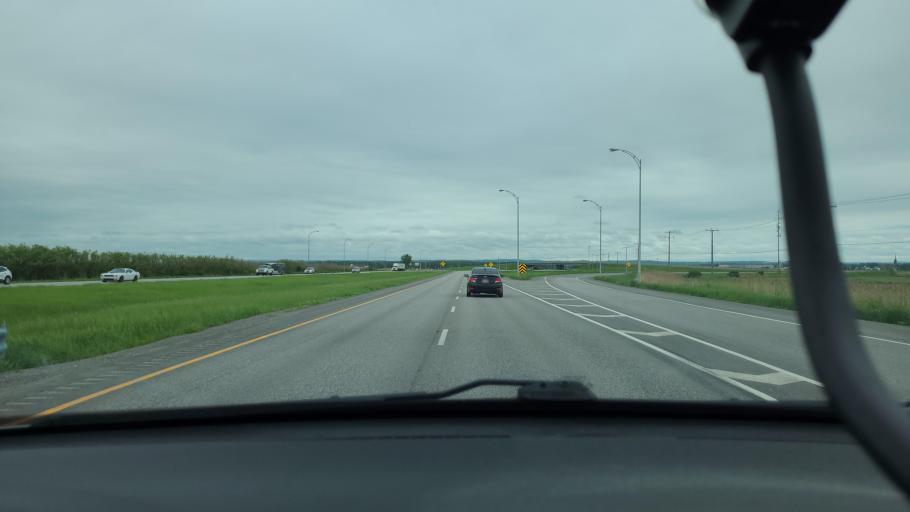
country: CA
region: Quebec
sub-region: Lanaudiere
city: Sainte-Julienne
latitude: 45.8808
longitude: -73.6551
